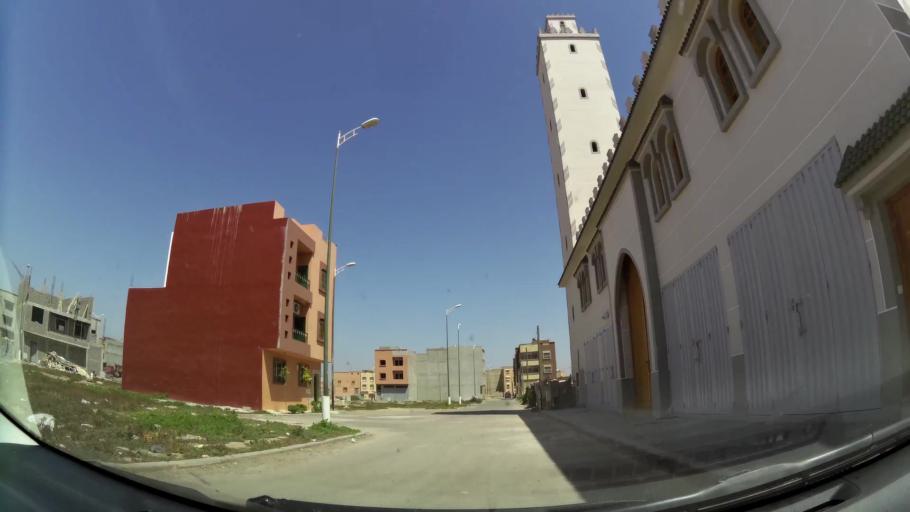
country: MA
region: Souss-Massa-Draa
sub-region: Inezgane-Ait Mellou
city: Inezgane
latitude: 30.3475
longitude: -9.5166
